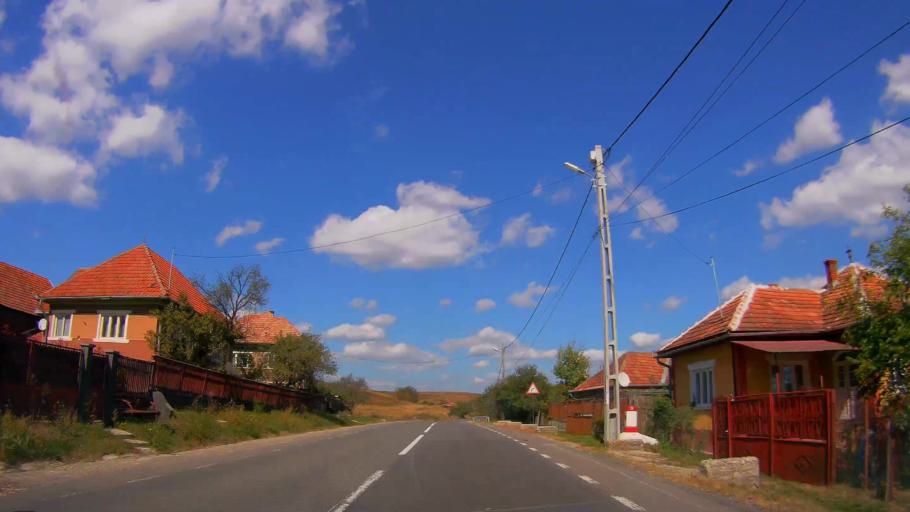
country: RO
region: Cluj
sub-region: Comuna Sanpaul
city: Sanpaul
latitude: 46.9089
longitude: 23.4169
